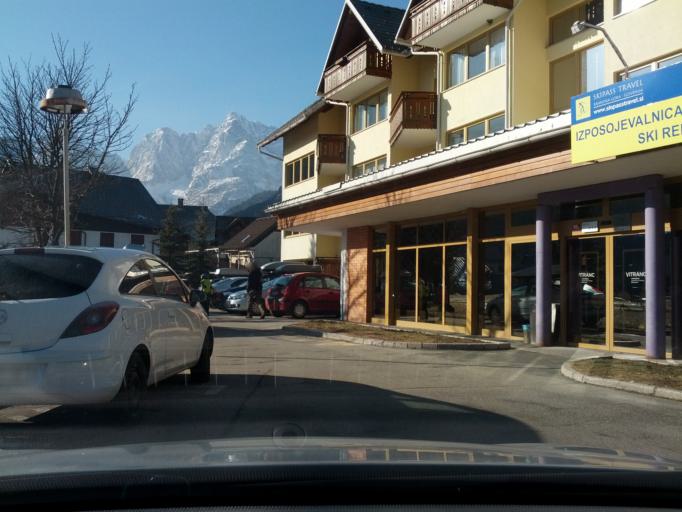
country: SI
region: Kranjska Gora
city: Kranjska Gora
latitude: 46.4839
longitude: 13.7821
